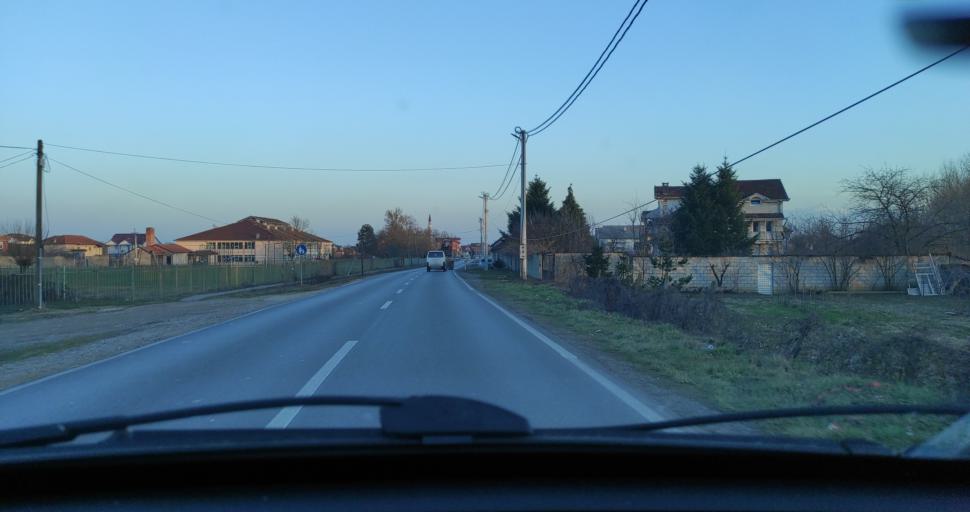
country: XK
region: Gjakova
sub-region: Komuna e Gjakoves
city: Gjakove
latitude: 42.4334
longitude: 20.3785
